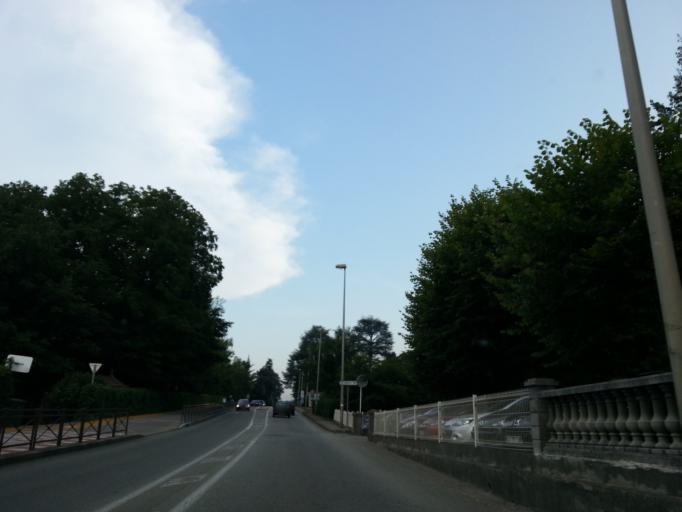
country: FR
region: Rhone-Alpes
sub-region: Departement de la Haute-Savoie
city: Sevrier
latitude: 45.8830
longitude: 6.1419
